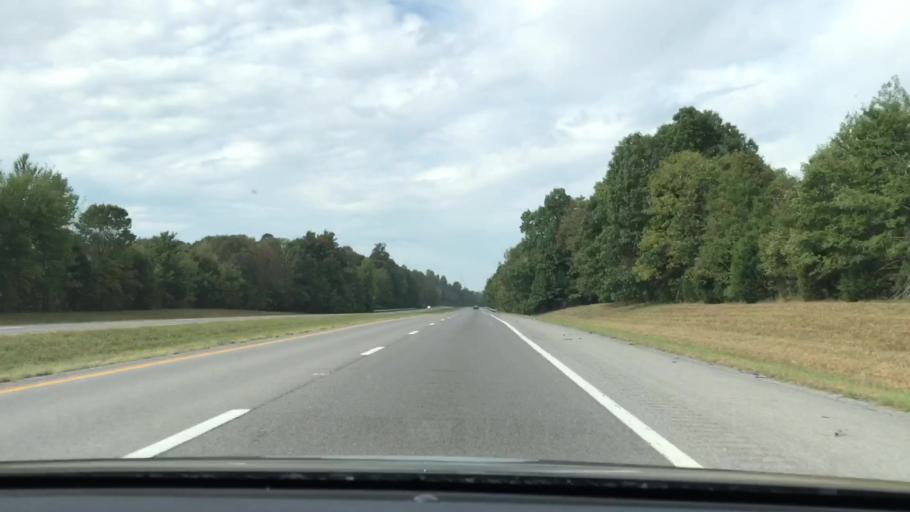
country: US
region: Kentucky
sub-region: Graves County
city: Mayfield
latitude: 36.7949
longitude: -88.5115
